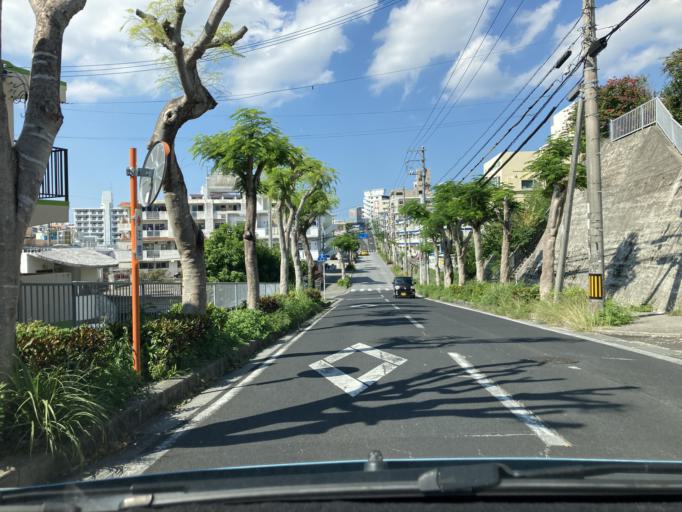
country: JP
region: Okinawa
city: Tomigusuku
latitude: 26.1978
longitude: 127.6999
